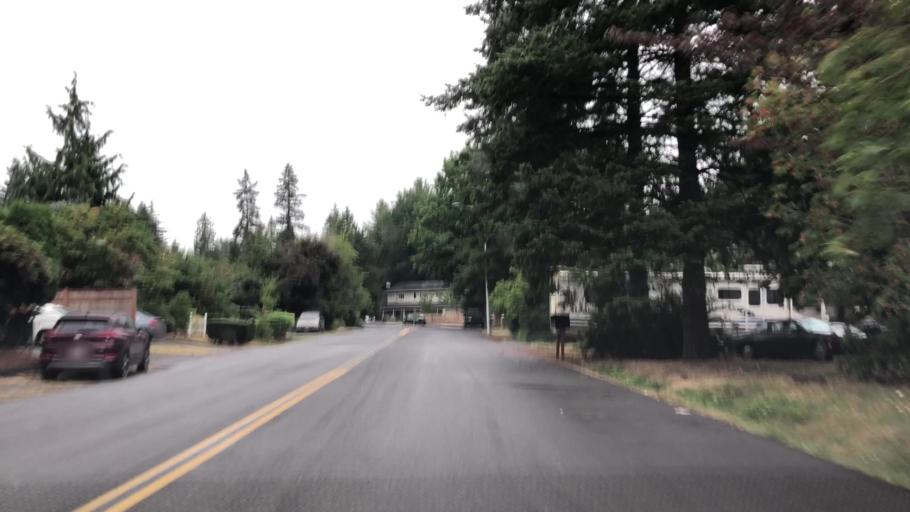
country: US
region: Washington
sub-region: Snohomish County
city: North Creek
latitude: 47.8121
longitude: -122.2134
